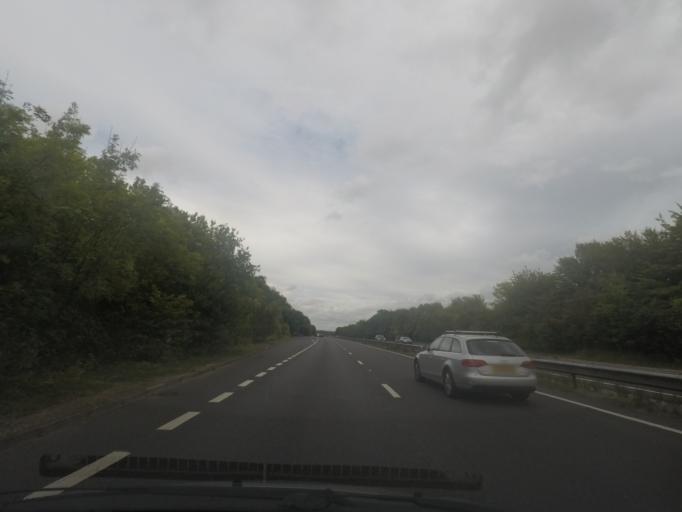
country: GB
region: England
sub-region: Wiltshire
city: Tidworth
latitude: 51.1992
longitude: -1.6171
